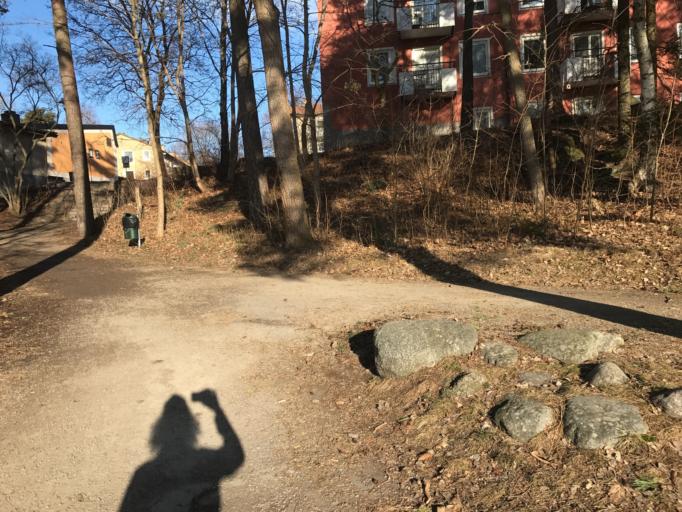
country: SE
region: Stockholm
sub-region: Nacka Kommun
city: Nacka
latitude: 59.2784
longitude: 18.1257
